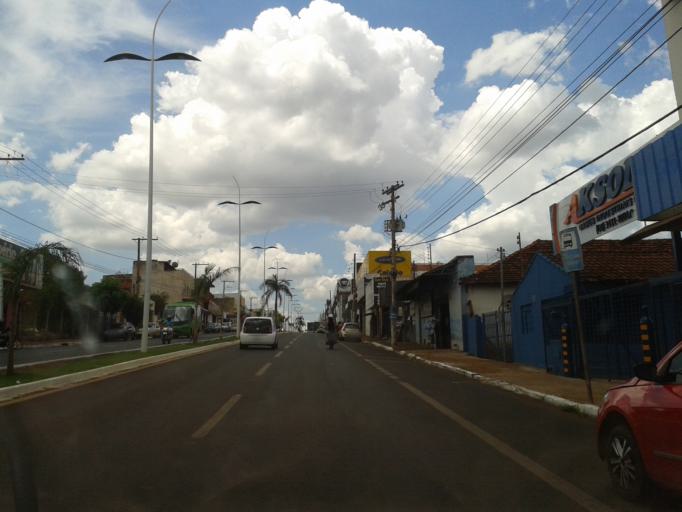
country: BR
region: Goias
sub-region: Itumbiara
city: Itumbiara
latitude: -18.4092
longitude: -49.2125
